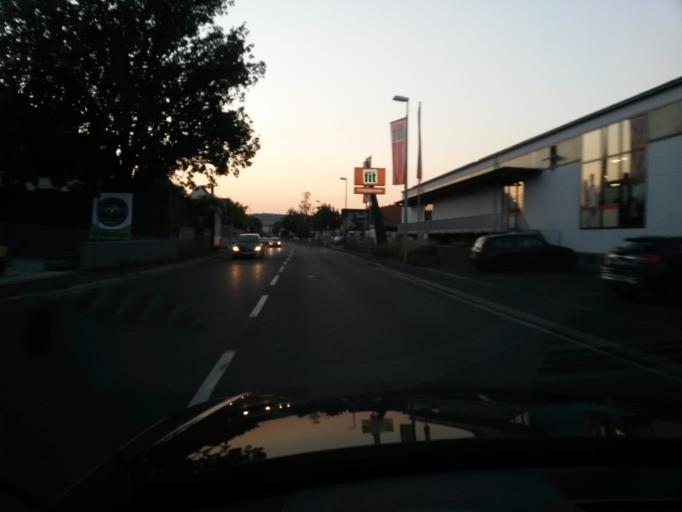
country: DE
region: Bavaria
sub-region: Regierungsbezirk Unterfranken
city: Randersacker
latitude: 49.7587
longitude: 9.9691
